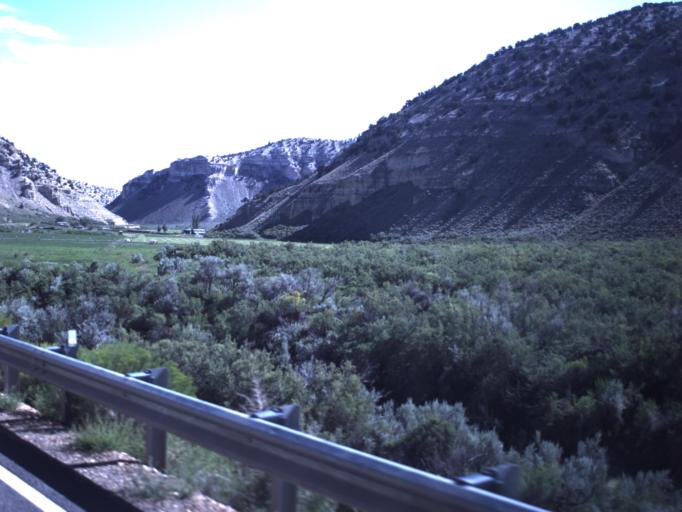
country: US
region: Utah
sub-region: Duchesne County
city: Duchesne
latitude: 40.0572
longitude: -110.5218
